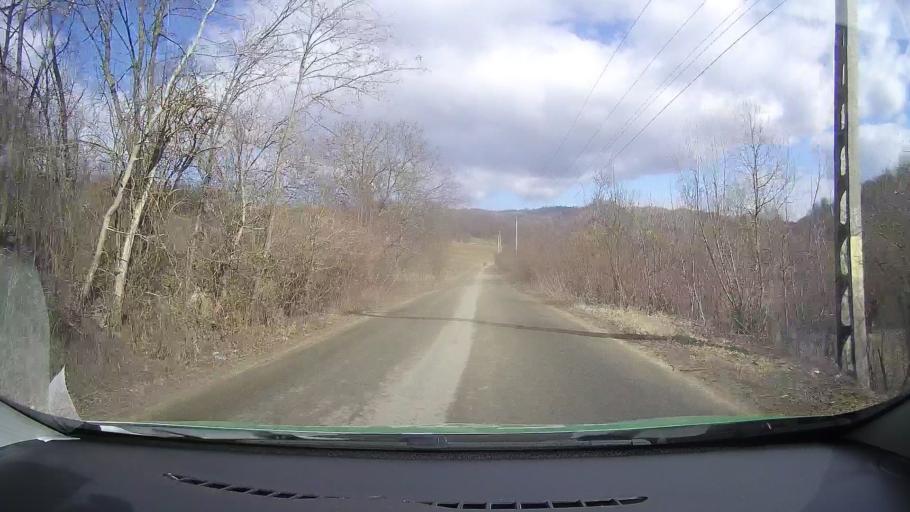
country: RO
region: Dambovita
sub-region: Comuna Motaeni
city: Motaeni
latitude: 45.1115
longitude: 25.4422
